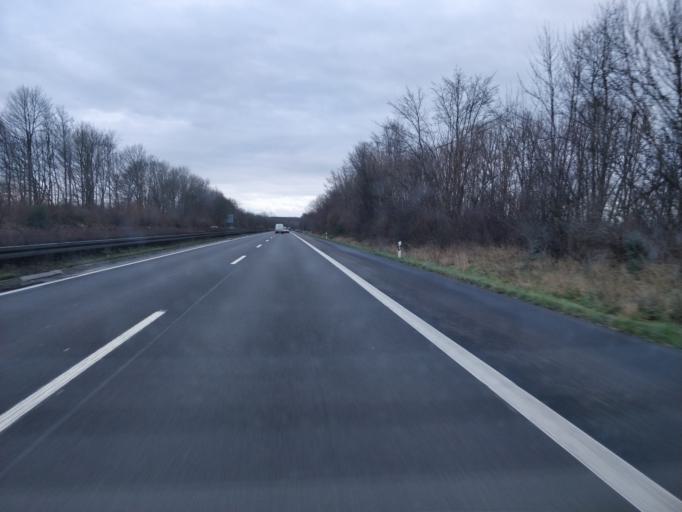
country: DE
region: North Rhine-Westphalia
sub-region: Regierungsbezirk Koln
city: Frechen
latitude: 50.8680
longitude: 6.8042
